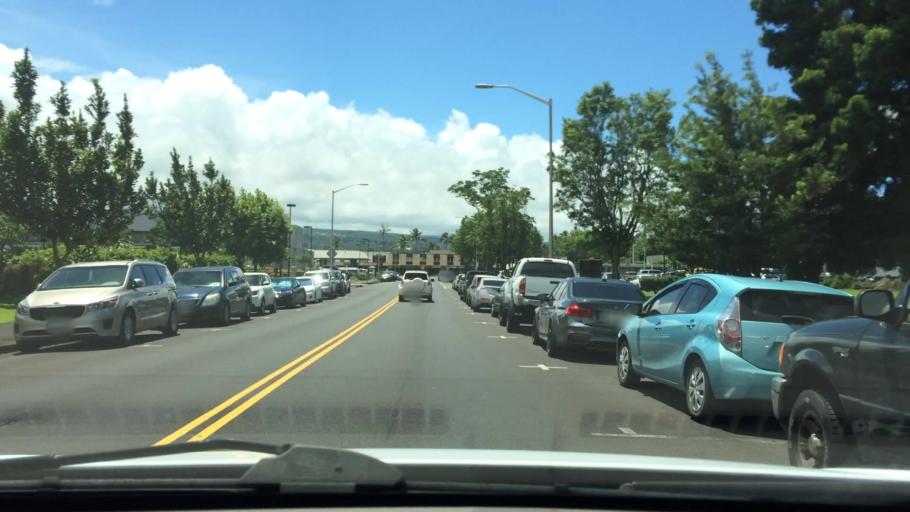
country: US
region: Hawaii
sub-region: Hawaii County
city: Hilo
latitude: 19.7182
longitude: -155.0776
